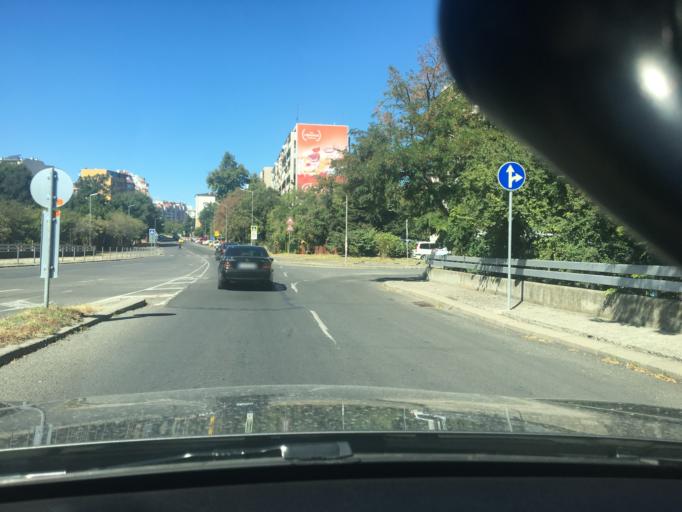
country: BG
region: Burgas
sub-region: Obshtina Burgas
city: Burgas
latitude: 42.5215
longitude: 27.4652
